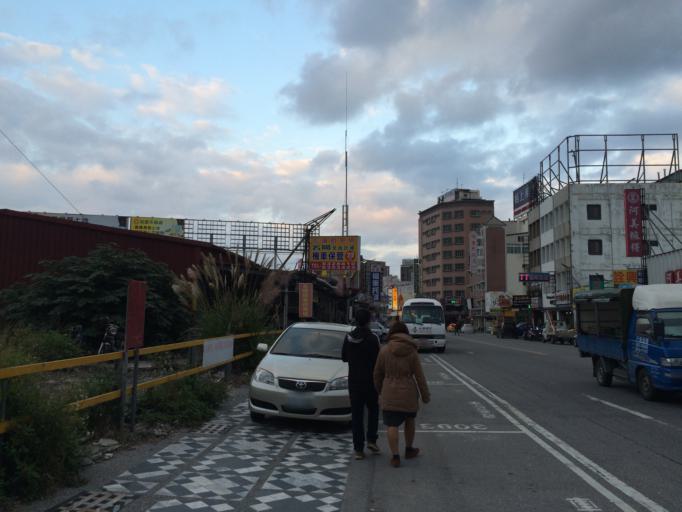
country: TW
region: Taiwan
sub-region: Hualien
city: Hualian
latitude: 23.9908
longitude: 121.6021
